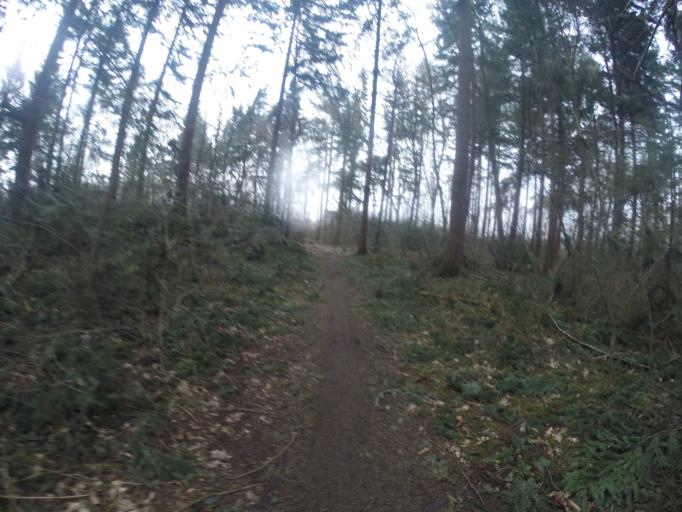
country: NL
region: Gelderland
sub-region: Gemeente Bronckhorst
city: Zelhem
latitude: 52.0074
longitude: 6.3606
